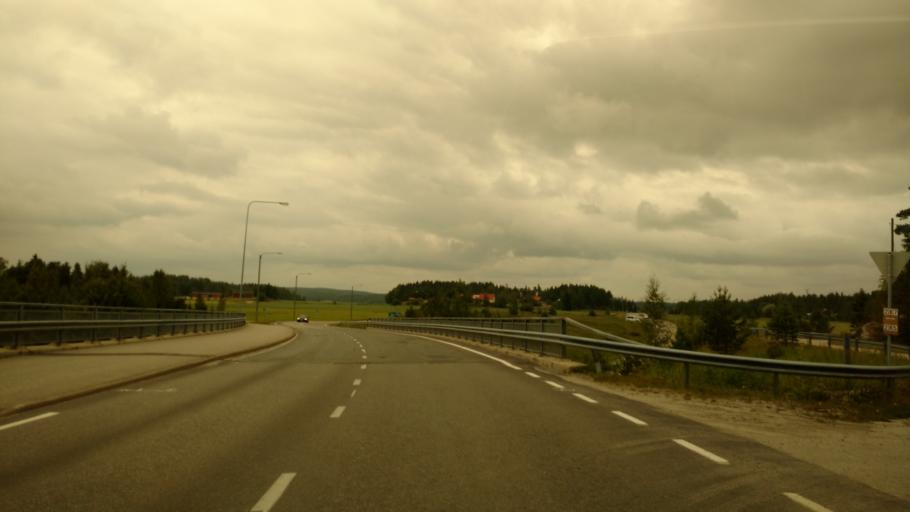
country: FI
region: Varsinais-Suomi
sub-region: Salo
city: Halikko
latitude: 60.4123
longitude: 23.0547
